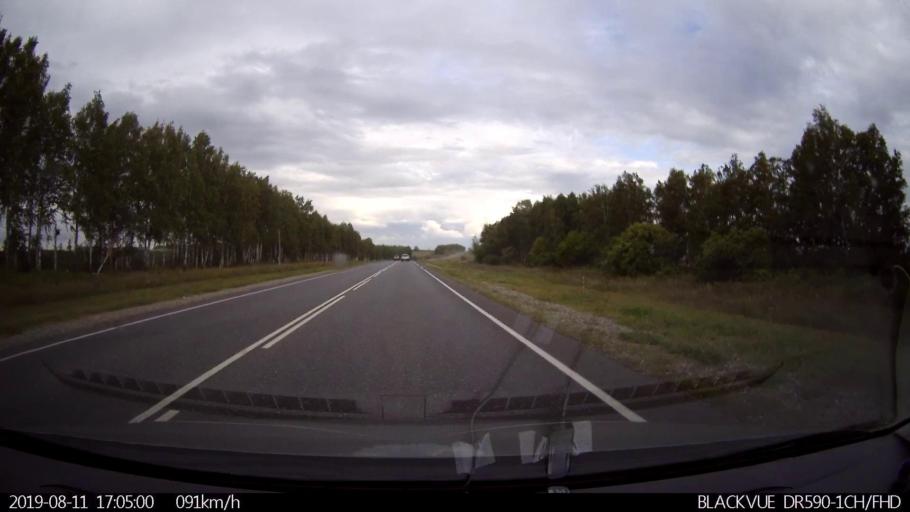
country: RU
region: Ulyanovsk
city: Mayna
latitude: 54.2996
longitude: 47.7764
